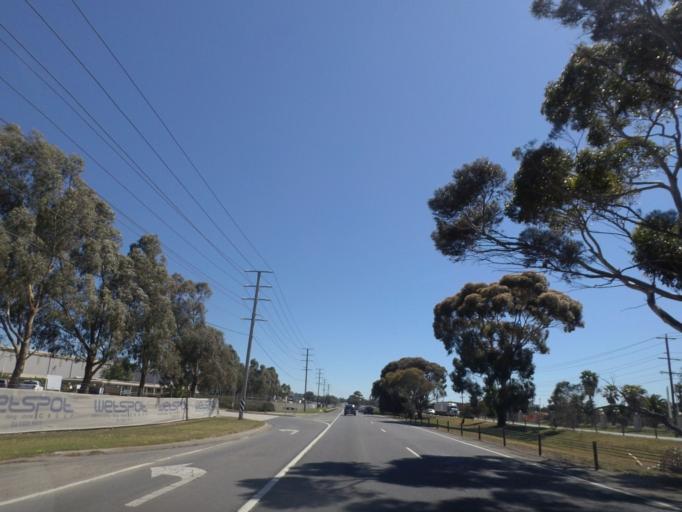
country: AU
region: Victoria
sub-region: Hume
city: Roxburgh Park
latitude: -37.6247
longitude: 144.9482
